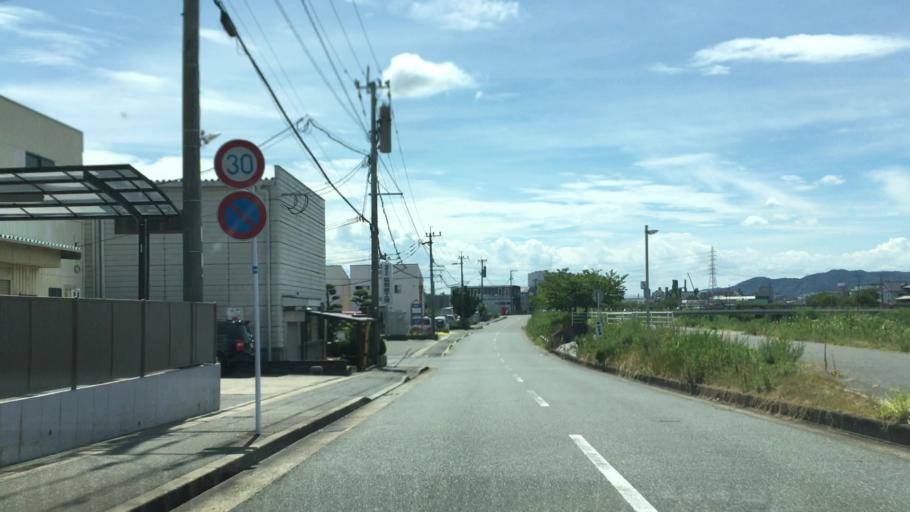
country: JP
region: Fukuoka
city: Onojo
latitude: 33.5449
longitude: 130.4808
